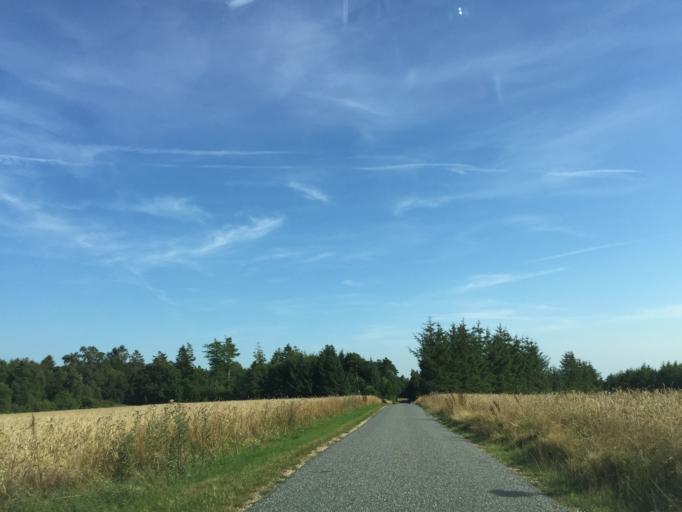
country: DK
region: Central Jutland
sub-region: Viborg Kommune
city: Bjerringbro
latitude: 56.2787
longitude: 9.6930
